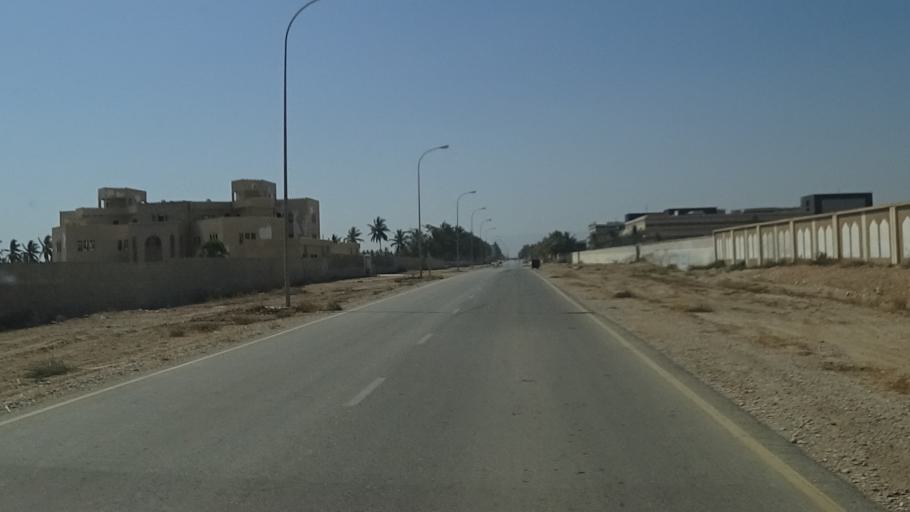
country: OM
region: Zufar
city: Salalah
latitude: 17.0338
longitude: 54.1693
